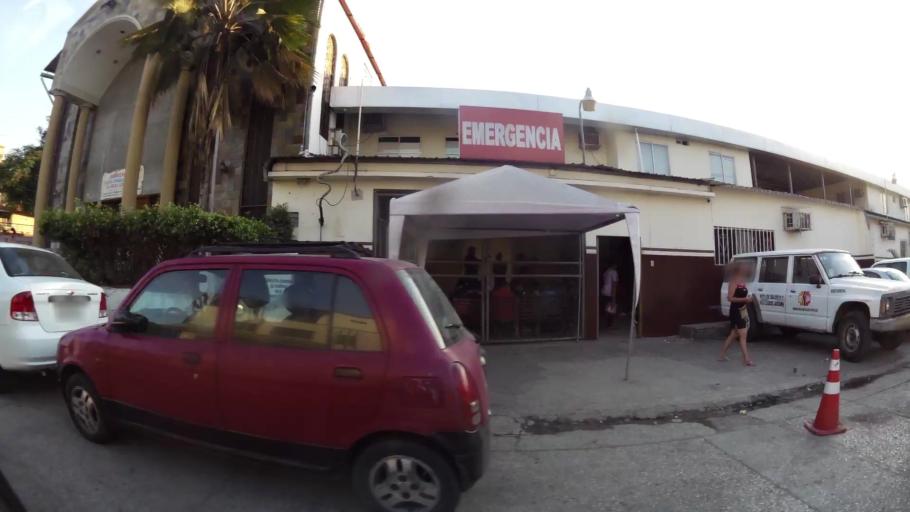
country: EC
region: Guayas
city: Guayaquil
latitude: -2.1455
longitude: -79.9226
